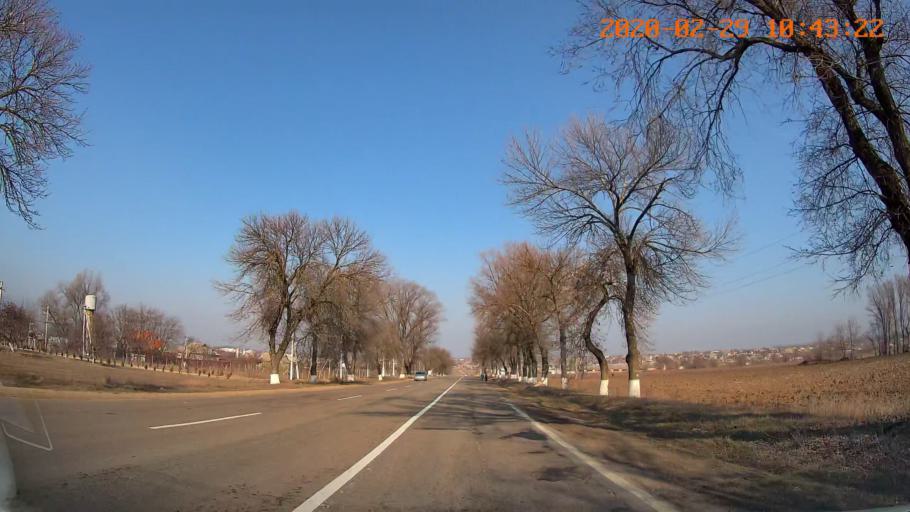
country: MD
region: Telenesti
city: Grigoriopol
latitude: 47.0605
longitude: 29.4038
